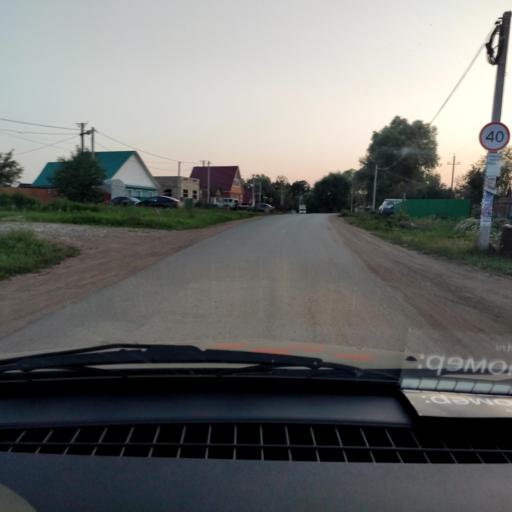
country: RU
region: Bashkortostan
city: Mikhaylovka
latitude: 54.7345
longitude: 55.8298
